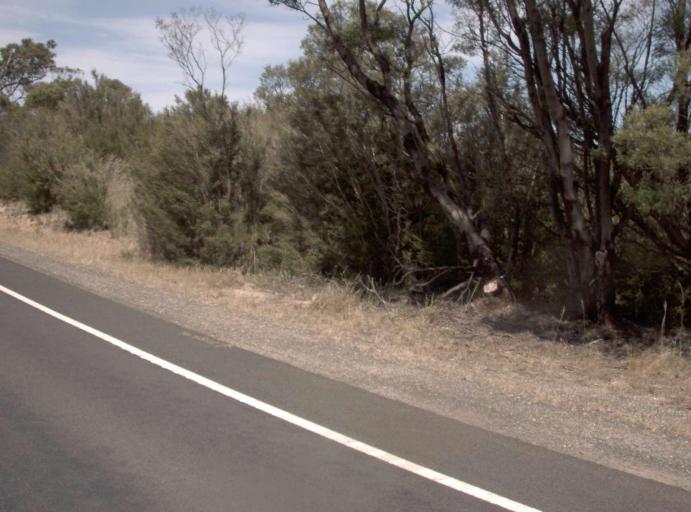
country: AU
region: Victoria
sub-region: Wellington
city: Heyfield
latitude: -38.1306
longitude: 146.8245
